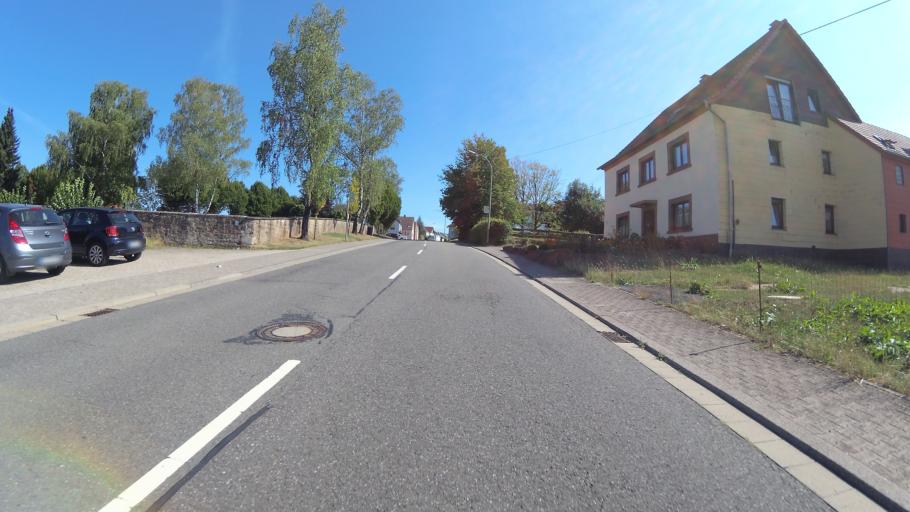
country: DE
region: Saarland
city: Eppelborn
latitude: 49.3678
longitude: 6.9818
